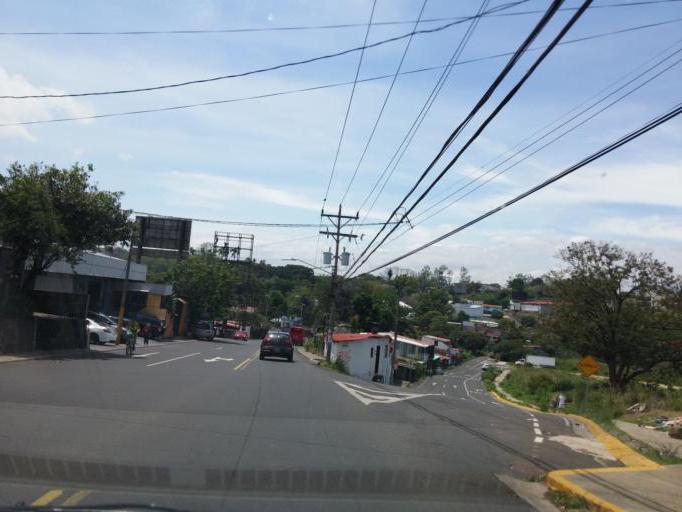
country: CR
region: Alajuela
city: Alajuela
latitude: 10.0044
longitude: -84.2039
